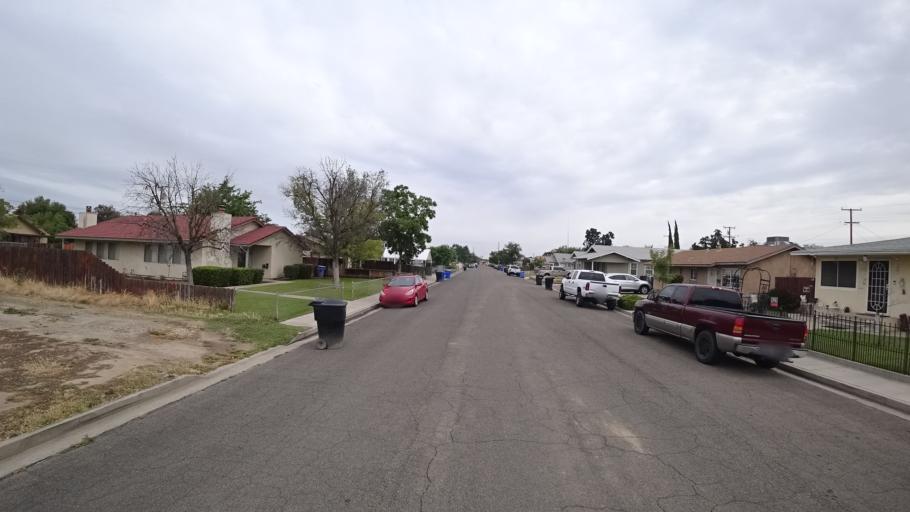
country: US
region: California
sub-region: Kings County
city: Hanford
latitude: 36.3395
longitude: -119.6399
